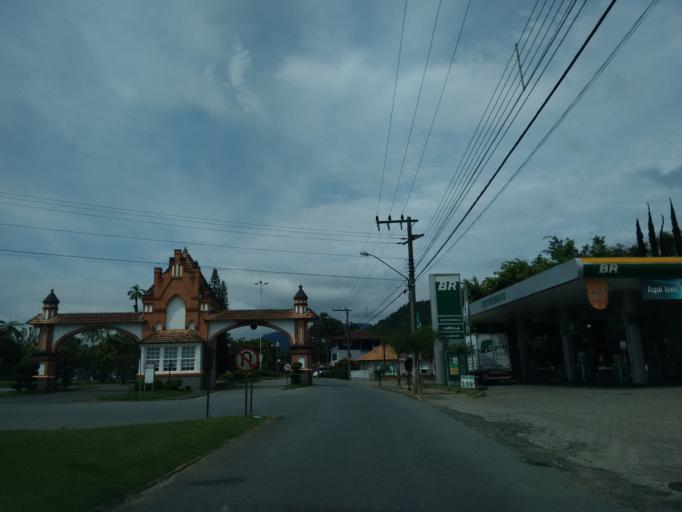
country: BR
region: Santa Catarina
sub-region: Pomerode
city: Pomerode
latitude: -26.7047
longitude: -49.1631
